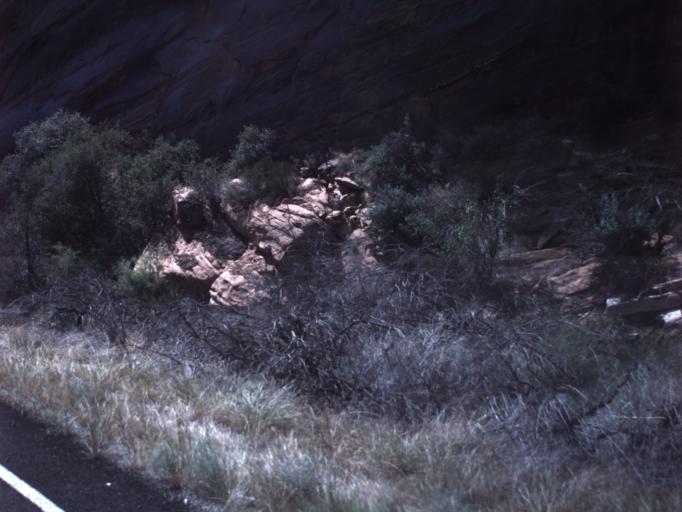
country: US
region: Utah
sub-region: Grand County
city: Moab
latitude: 38.5692
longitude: -109.5809
